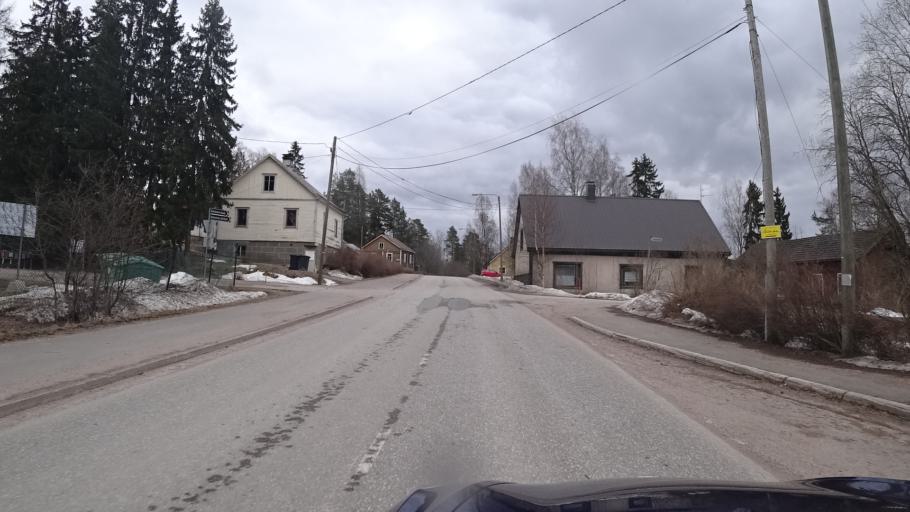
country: FI
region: Paijanne Tavastia
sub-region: Lahti
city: Nastola
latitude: 60.8747
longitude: 26.0033
